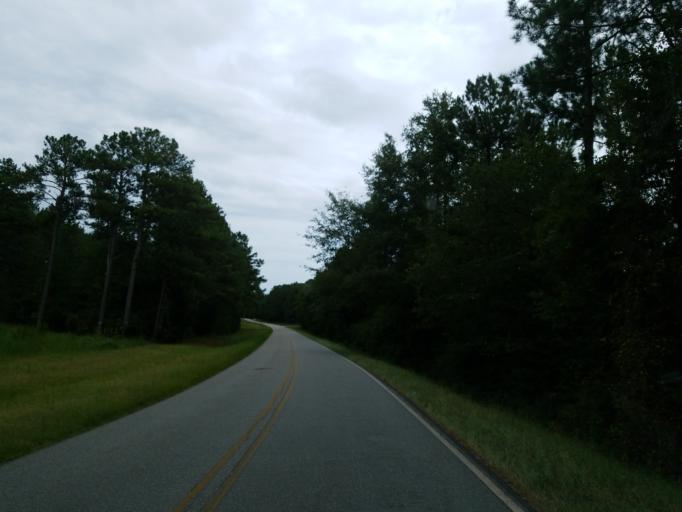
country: US
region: Georgia
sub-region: Monroe County
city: Forsyth
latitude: 32.9463
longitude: -83.9474
